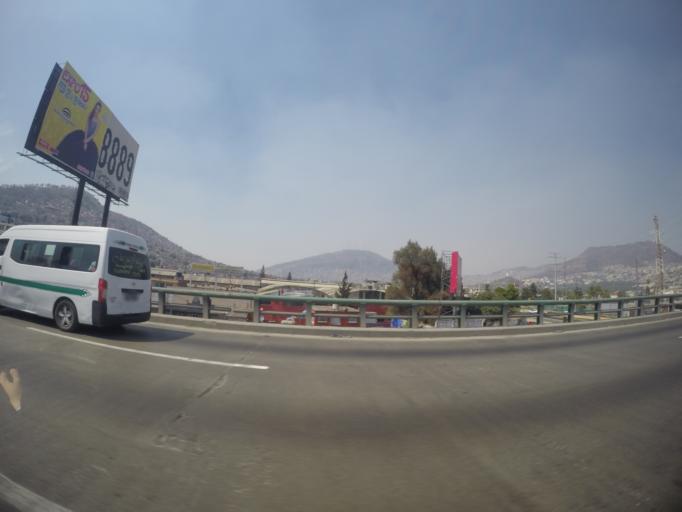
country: MX
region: Mexico City
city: Gustavo A. Madero
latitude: 19.5142
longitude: -99.1017
